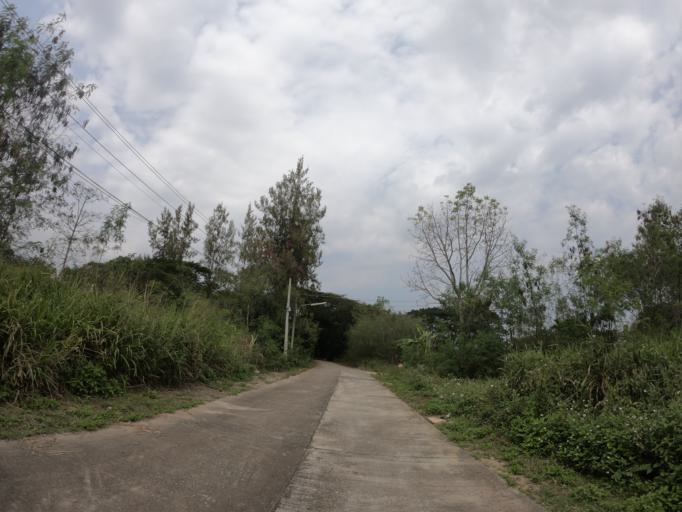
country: TH
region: Chiang Mai
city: Chiang Mai
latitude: 18.7570
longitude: 98.9798
